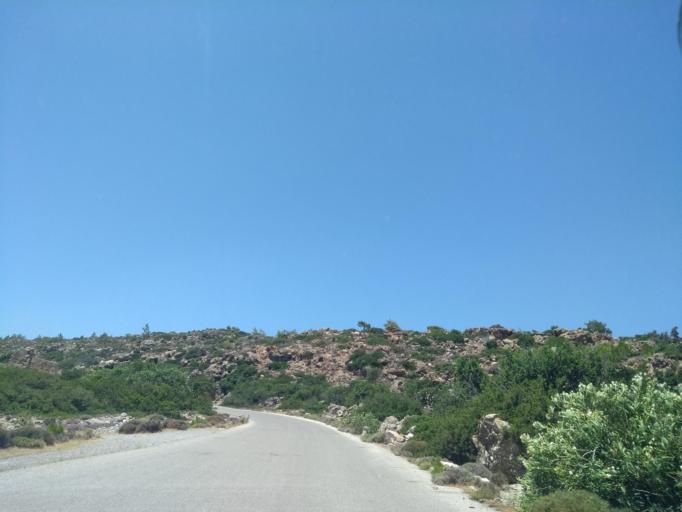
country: GR
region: Crete
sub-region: Nomos Chanias
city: Vryses
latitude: 35.3301
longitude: 23.5483
